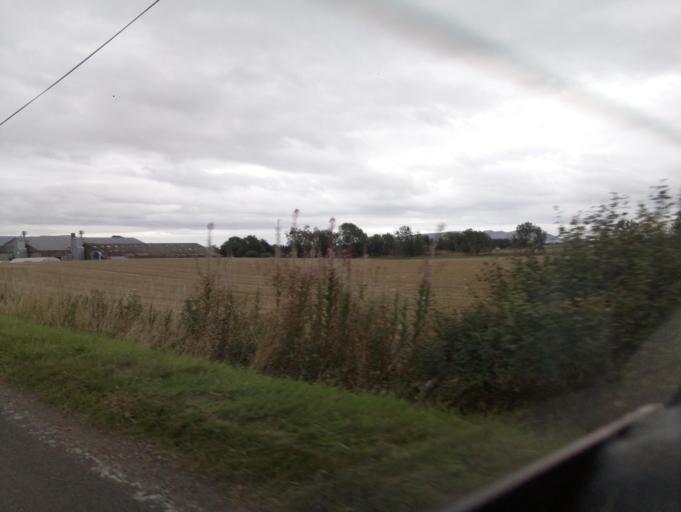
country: GB
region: Scotland
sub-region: Perth and Kinross
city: Kinross
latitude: 56.2169
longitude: -3.4738
